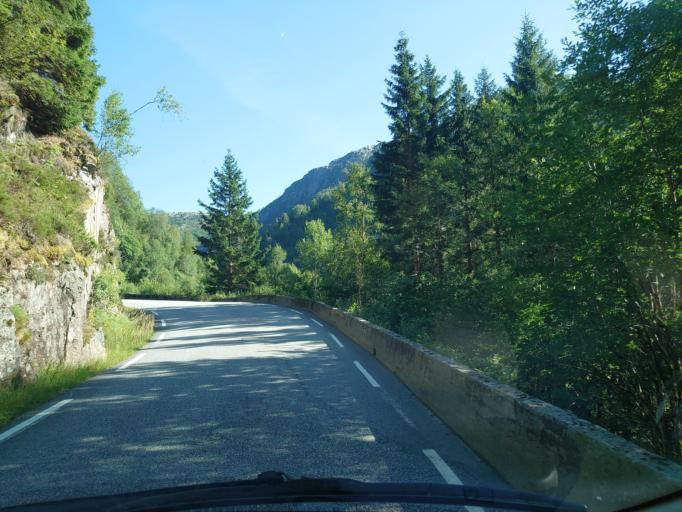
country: NO
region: Hordaland
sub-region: Vaksdal
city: Dale
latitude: 60.5850
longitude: 5.8565
